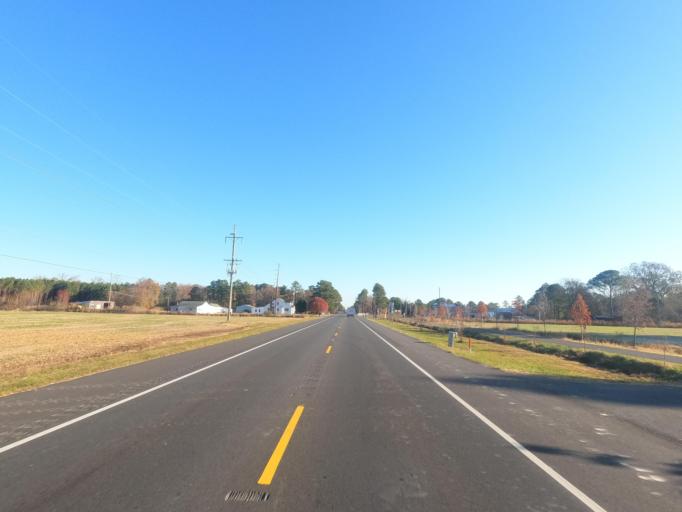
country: US
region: Maryland
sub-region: Somerset County
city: Crisfield
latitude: 38.0042
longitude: -75.8244
